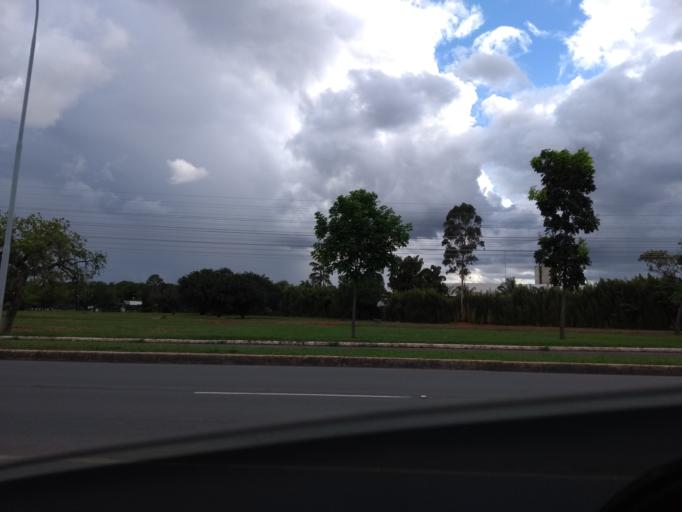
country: BR
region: Federal District
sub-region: Brasilia
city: Brasilia
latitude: -15.8113
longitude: -47.9187
